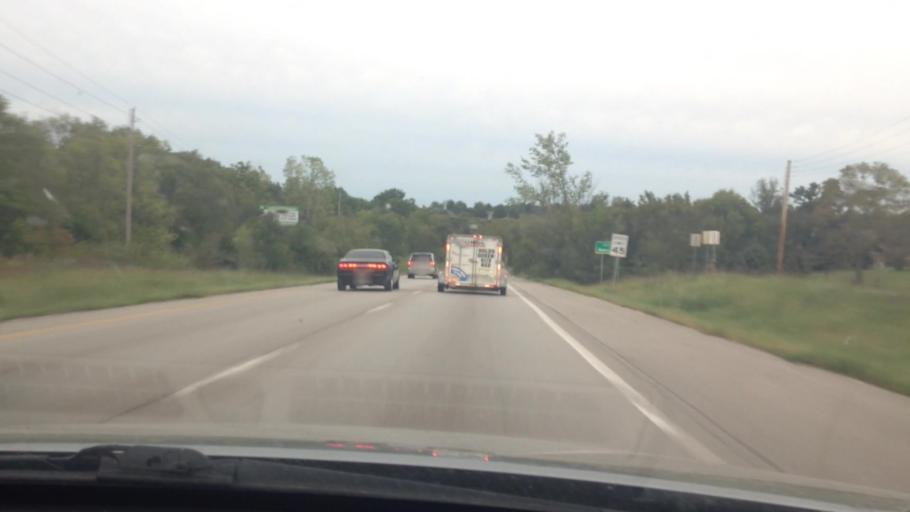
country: US
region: Missouri
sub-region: Jackson County
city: Raytown
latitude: 38.9714
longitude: -94.4420
